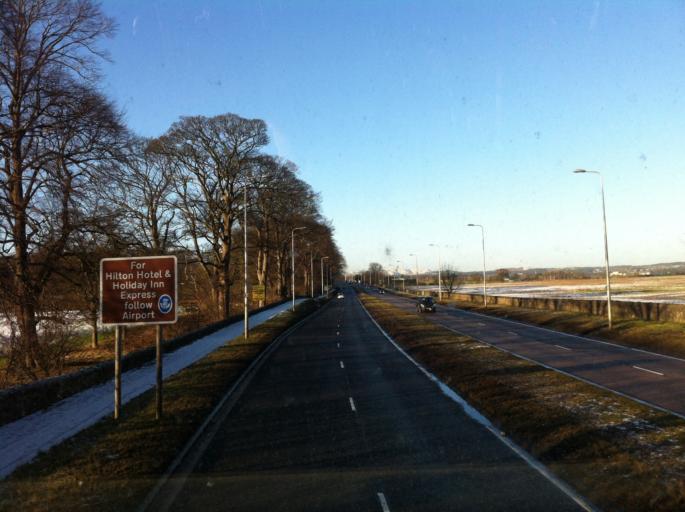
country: GB
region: Scotland
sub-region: Edinburgh
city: Ratho
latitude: 55.9364
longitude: -3.3424
